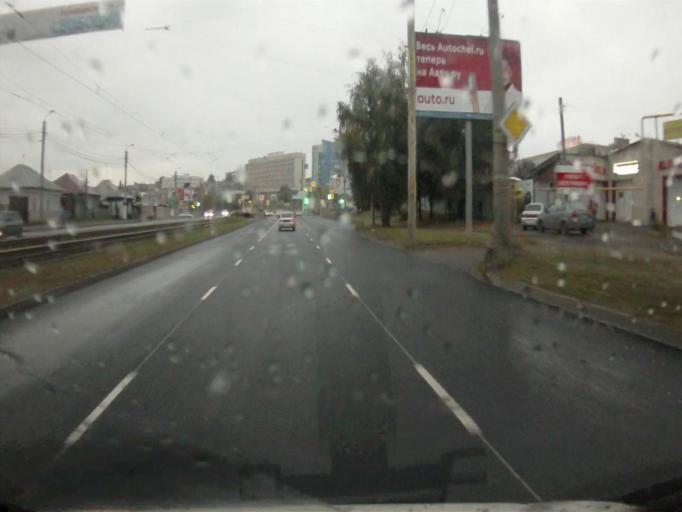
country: RU
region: Chelyabinsk
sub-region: Gorod Chelyabinsk
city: Chelyabinsk
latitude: 55.1872
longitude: 61.3628
